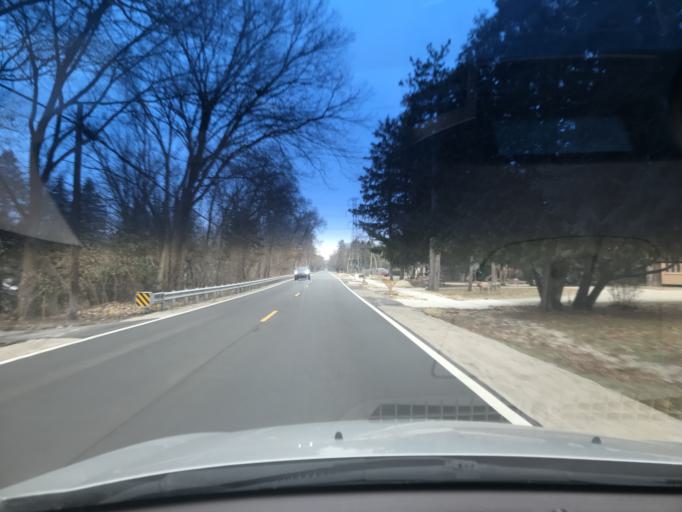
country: US
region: Michigan
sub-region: Macomb County
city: Shelby
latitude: 42.6601
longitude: -83.0554
